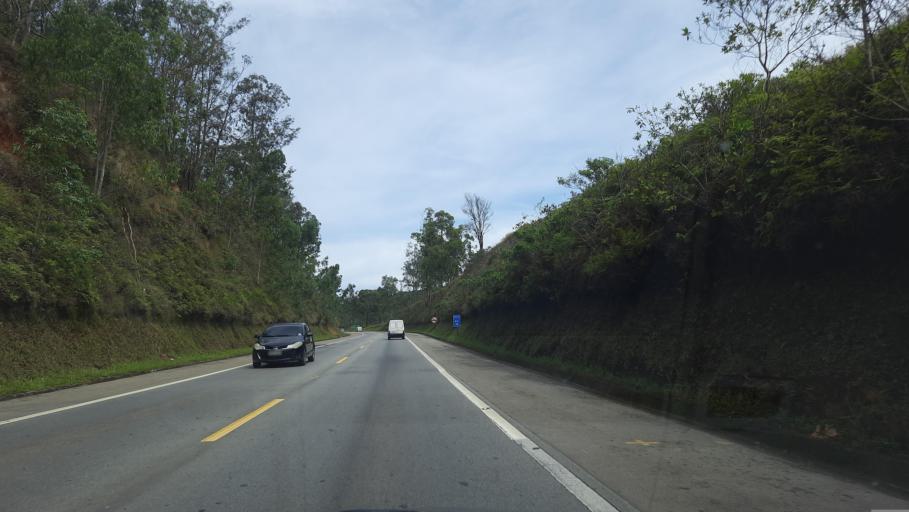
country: BR
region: Sao Paulo
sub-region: Franco Da Rocha
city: Franco da Rocha
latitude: -23.3360
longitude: -46.6639
